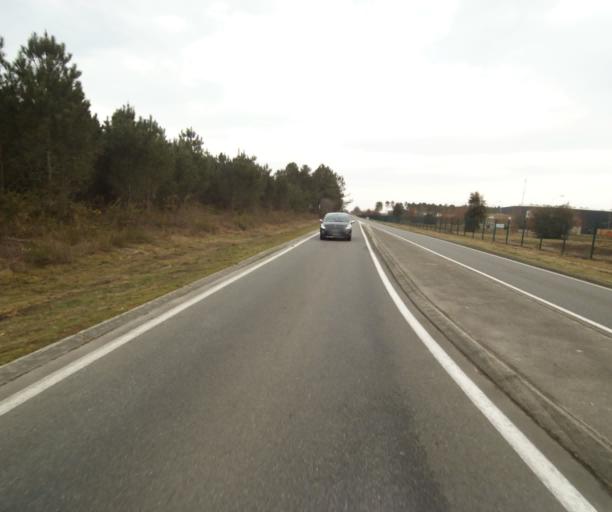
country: FR
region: Aquitaine
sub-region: Departement des Landes
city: Gabarret
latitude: 44.0775
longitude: -0.0396
